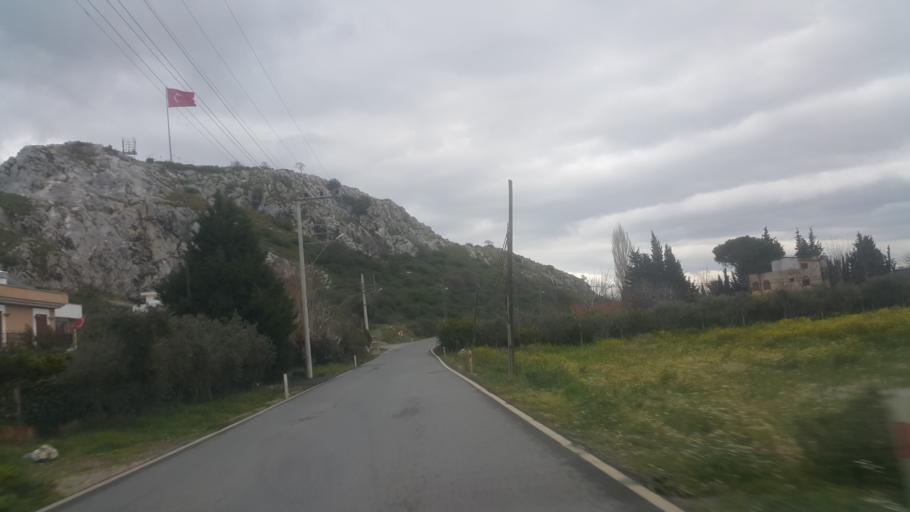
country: TR
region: Izmir
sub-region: Seferihisar
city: Seferhisar
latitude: 38.1905
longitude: 26.8048
